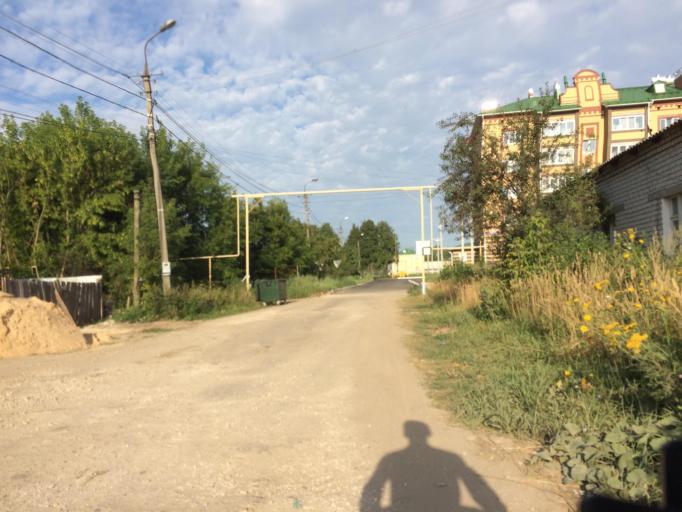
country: RU
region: Mariy-El
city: Medvedevo
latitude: 56.6352
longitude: 47.8131
